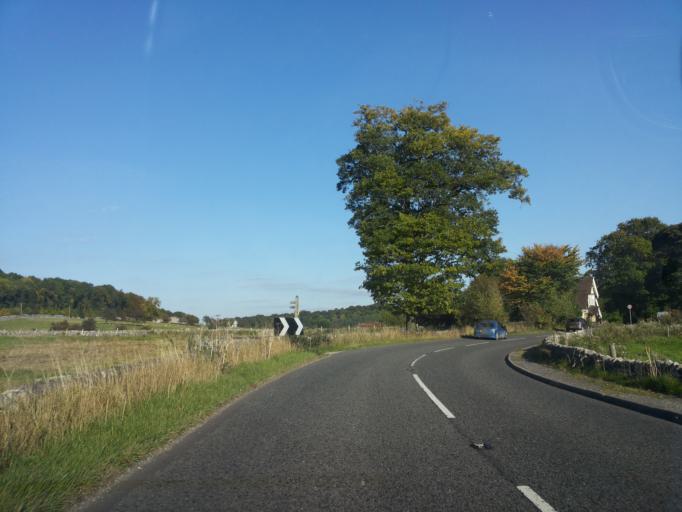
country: GB
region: England
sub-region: Derbyshire
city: Bakewell
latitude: 53.2344
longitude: -1.6828
